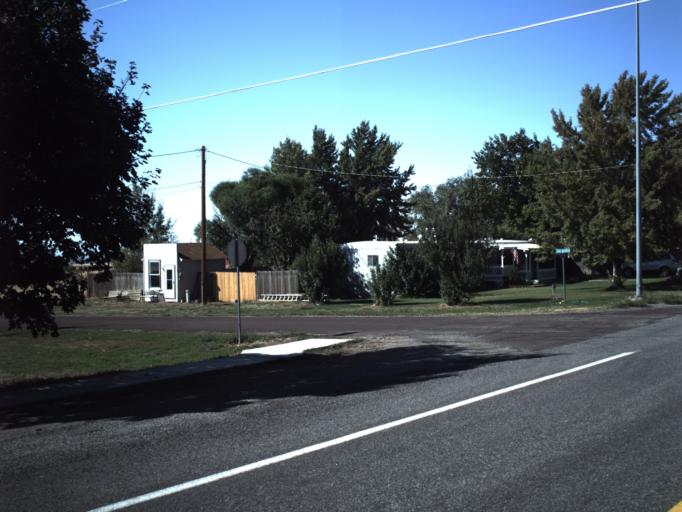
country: US
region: Utah
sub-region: Millard County
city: Fillmore
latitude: 39.1040
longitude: -112.2709
